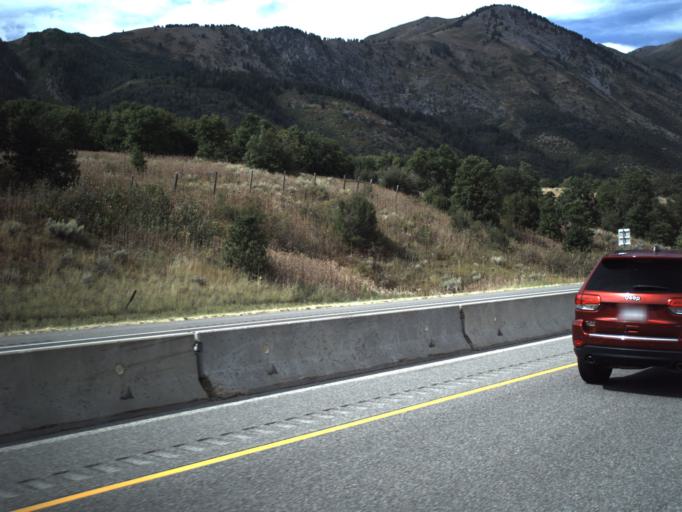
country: US
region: Utah
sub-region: Cache County
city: Wellsville
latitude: 41.5882
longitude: -111.9763
